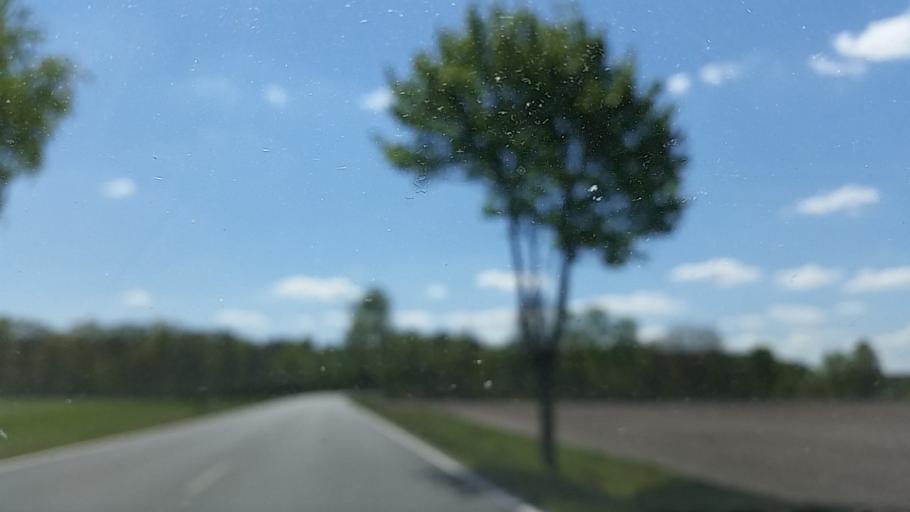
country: DE
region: Lower Saxony
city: Schneverdingen
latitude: 53.1612
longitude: 9.8091
